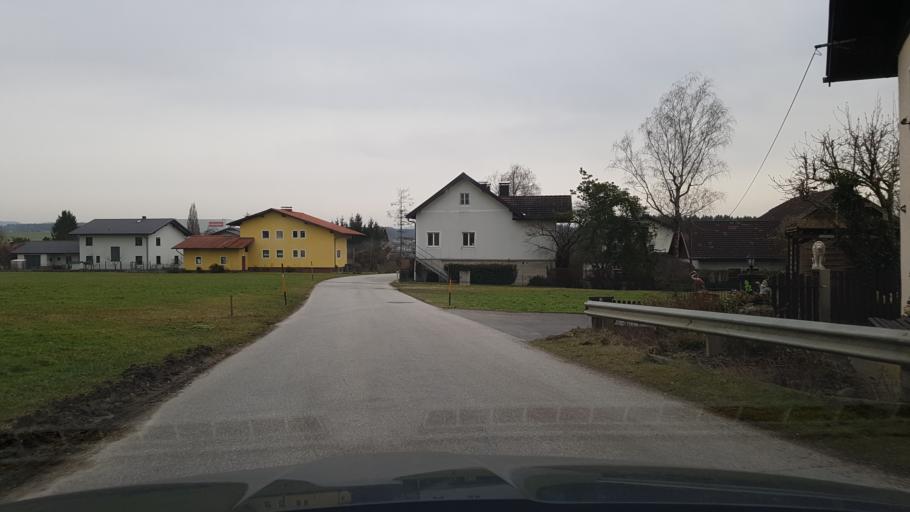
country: AT
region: Salzburg
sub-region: Politischer Bezirk Salzburg-Umgebung
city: Lamprechtshausen
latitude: 48.0096
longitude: 12.9601
